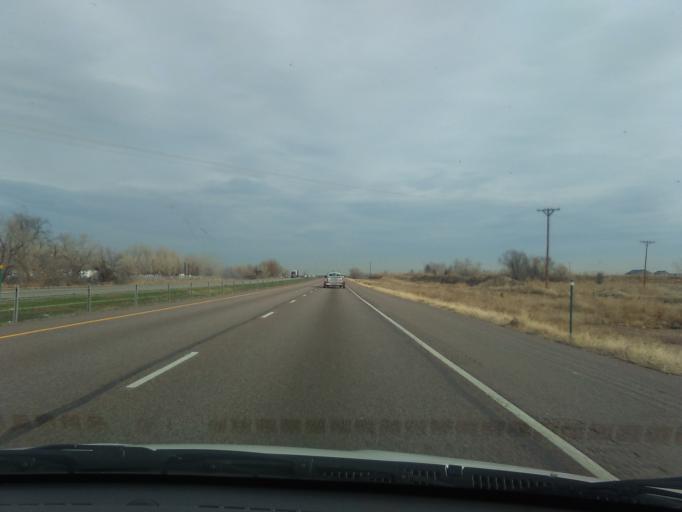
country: US
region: Colorado
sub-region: Adams County
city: Todd Creek
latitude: 39.8994
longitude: -104.8422
